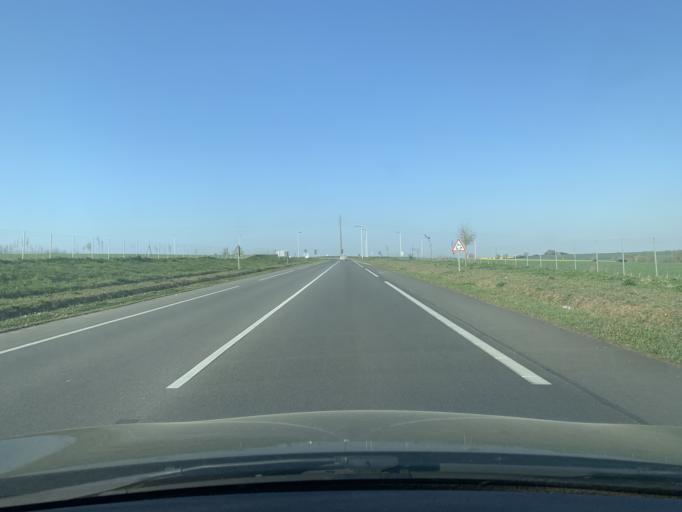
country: FR
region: Nord-Pas-de-Calais
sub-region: Departement du Nord
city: Escaudoeuvres
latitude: 50.1580
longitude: 3.2977
